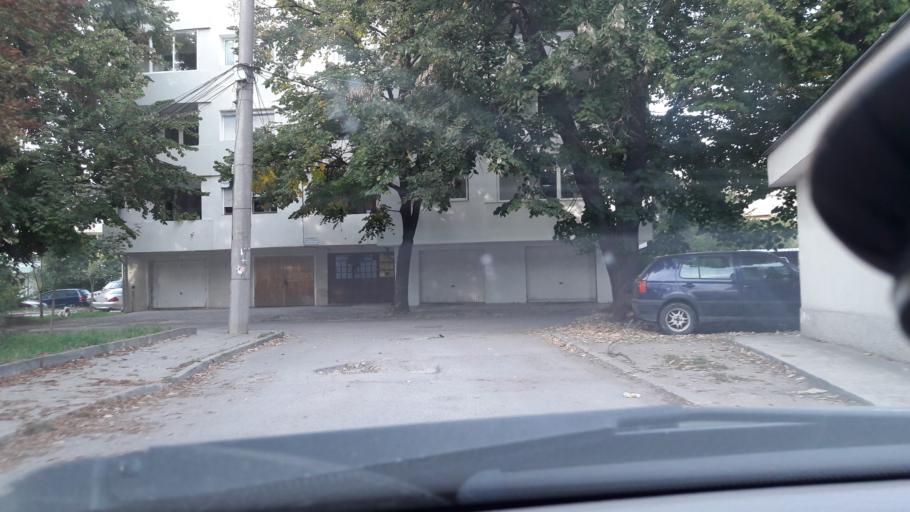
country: BG
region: Razgrad
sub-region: Obshtina Razgrad
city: Razgrad
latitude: 43.5286
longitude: 26.5258
